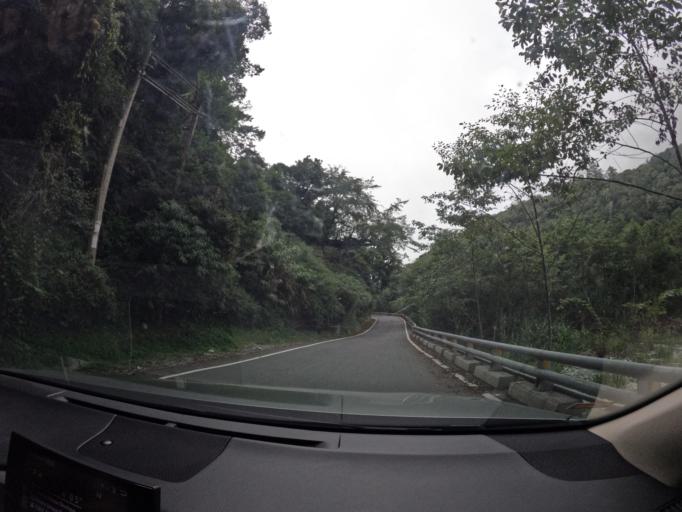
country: TW
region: Taiwan
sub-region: Taitung
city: Taitung
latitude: 23.2474
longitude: 120.9914
